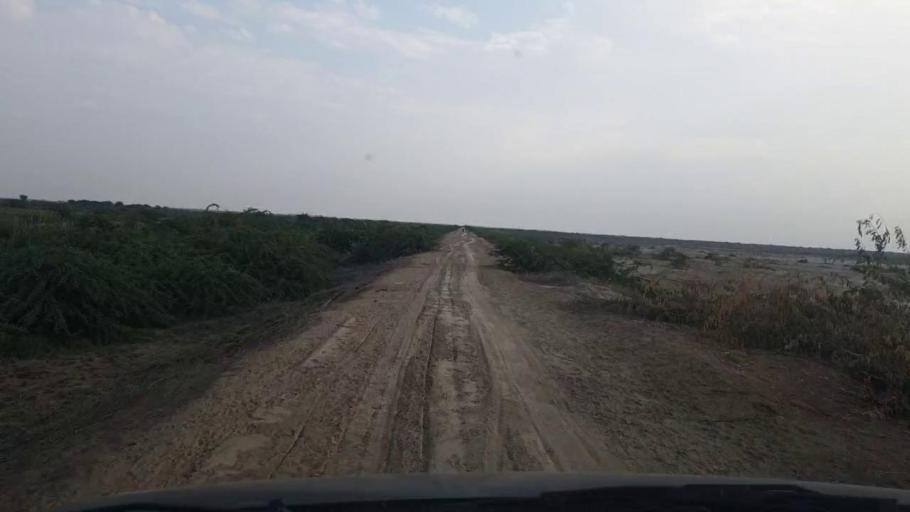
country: PK
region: Sindh
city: Badin
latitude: 24.4822
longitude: 68.6980
